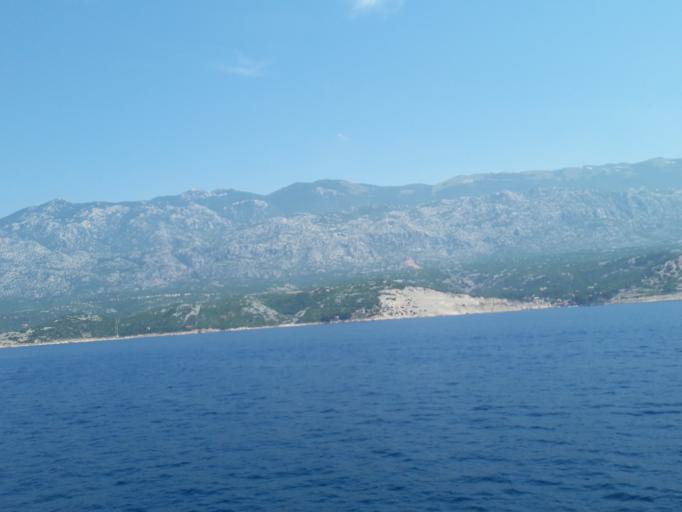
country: HR
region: Primorsko-Goranska
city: Banjol
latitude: 44.7040
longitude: 14.8713
